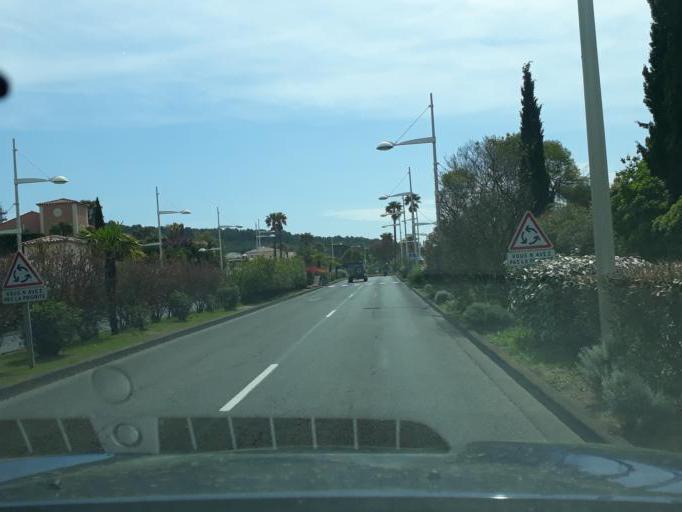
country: FR
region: Languedoc-Roussillon
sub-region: Departement de l'Herault
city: Agde
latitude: 43.3002
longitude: 3.4910
